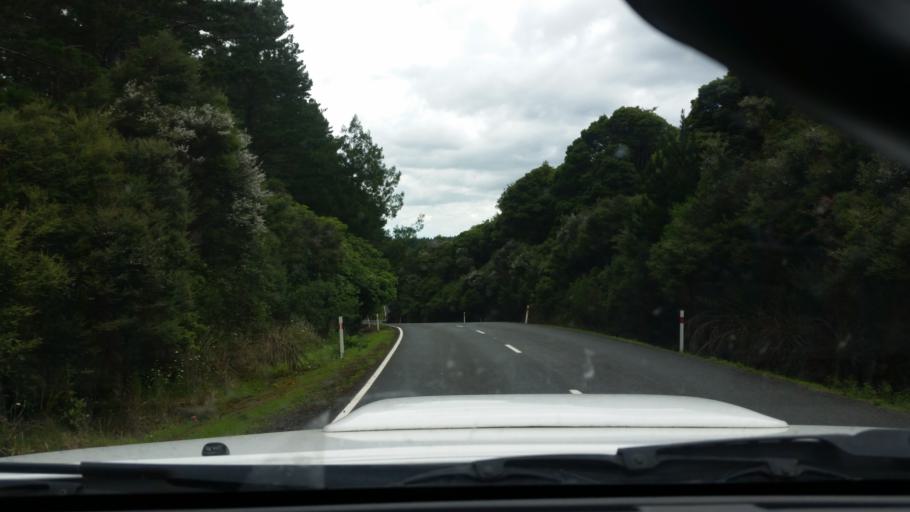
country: NZ
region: Northland
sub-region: Kaipara District
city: Dargaville
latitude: -35.7308
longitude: 173.8624
